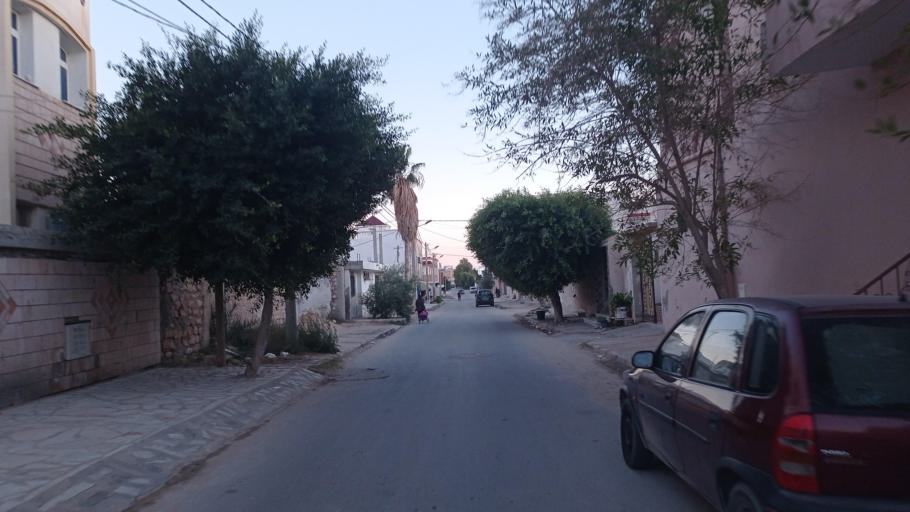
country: TN
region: Qabis
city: Gabes
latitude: 33.8468
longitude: 10.1144
